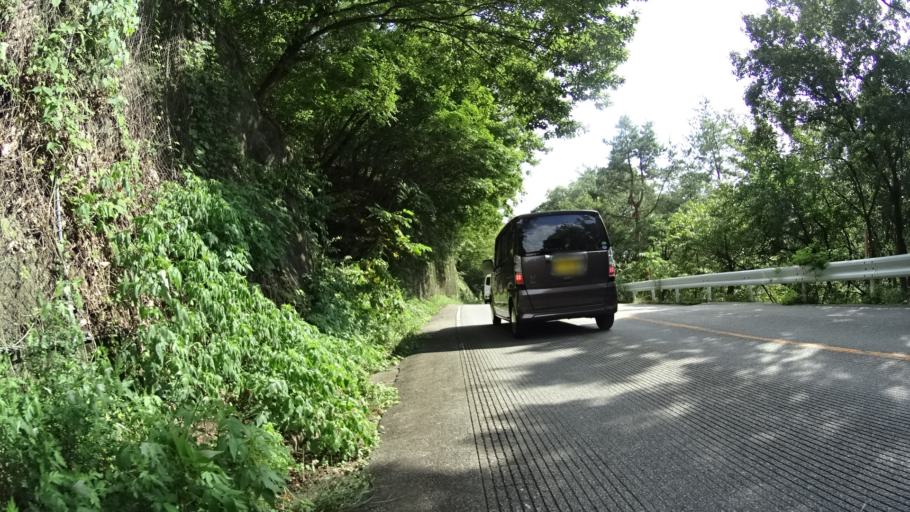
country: JP
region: Yamanashi
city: Kofu-shi
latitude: 35.7158
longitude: 138.5535
